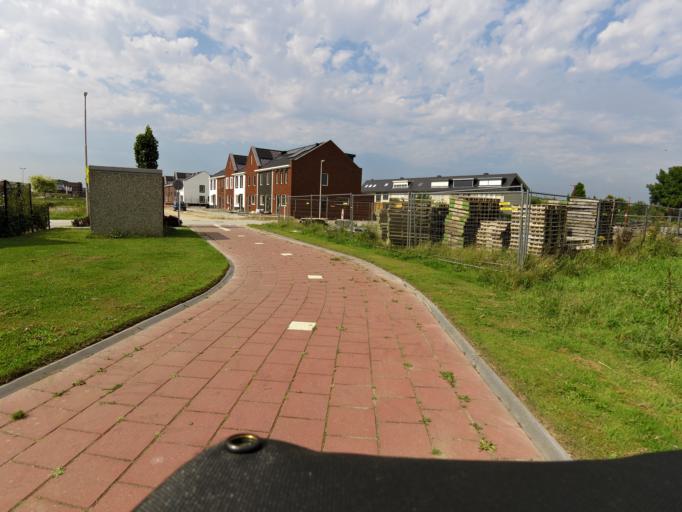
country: NL
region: South Holland
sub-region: Gemeente Oud-Beijerland
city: Oud-Beijerland
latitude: 51.8125
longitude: 4.4359
